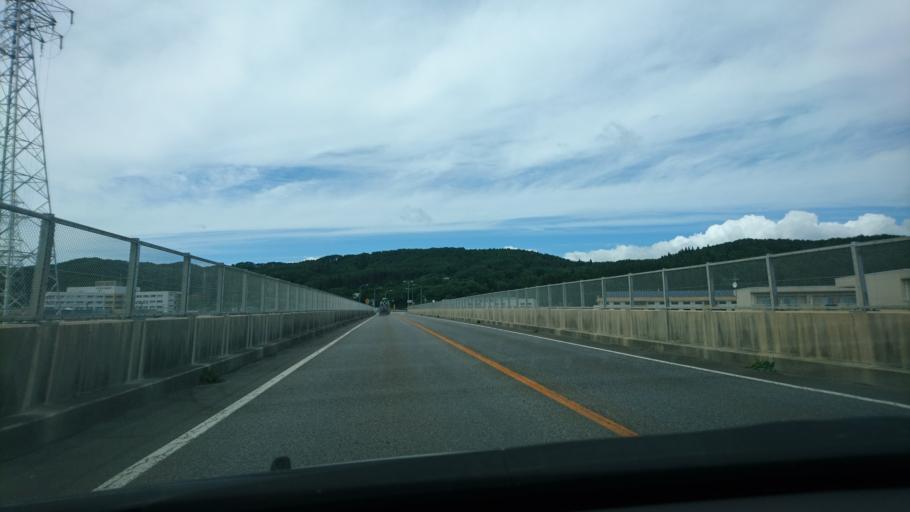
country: JP
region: Aomori
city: Hachinohe
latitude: 40.1973
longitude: 141.7822
